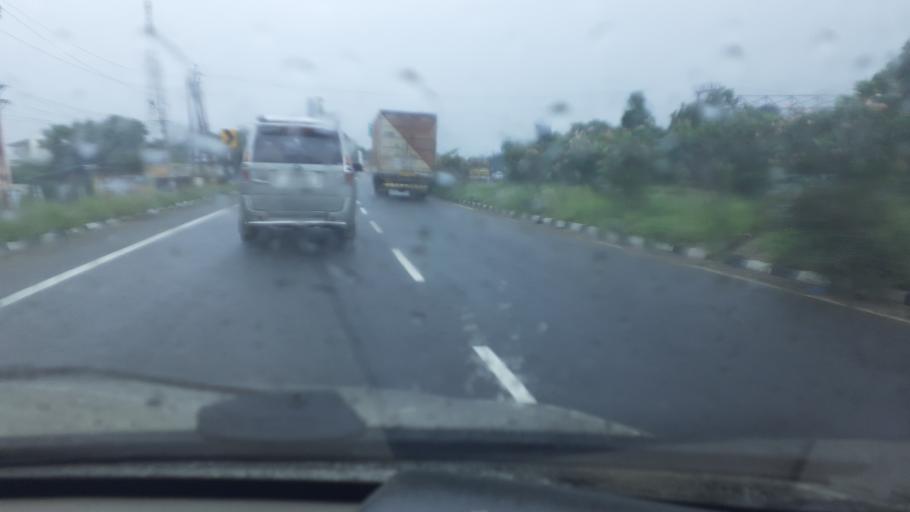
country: IN
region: Tamil Nadu
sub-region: Virudhunagar
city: Virudunagar
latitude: 9.6109
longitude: 77.9566
